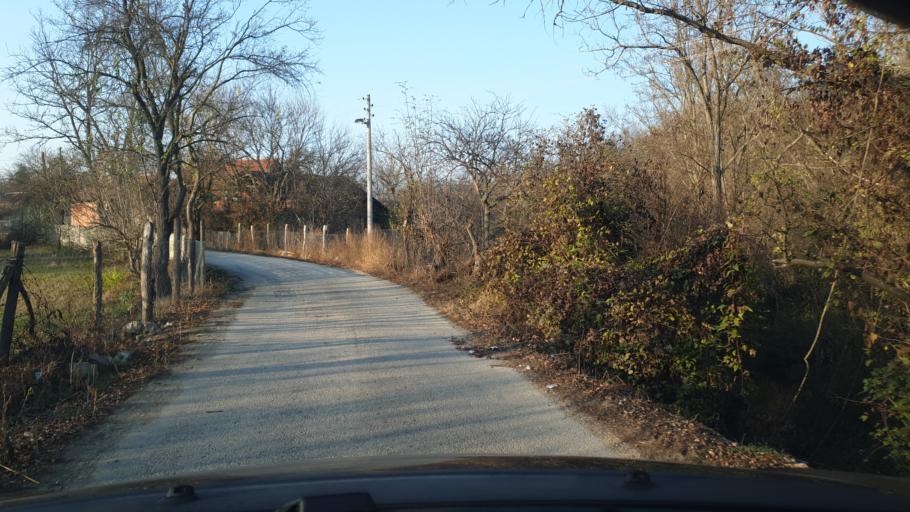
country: RS
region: Central Serbia
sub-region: Zajecarski Okrug
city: Zajecar
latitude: 44.0309
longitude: 22.3290
